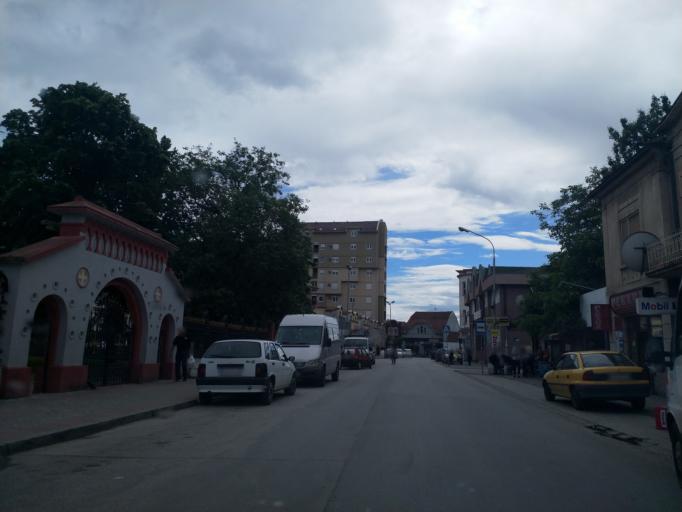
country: RS
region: Central Serbia
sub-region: Pomoravski Okrug
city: Jagodina
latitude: 43.9810
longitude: 21.2599
